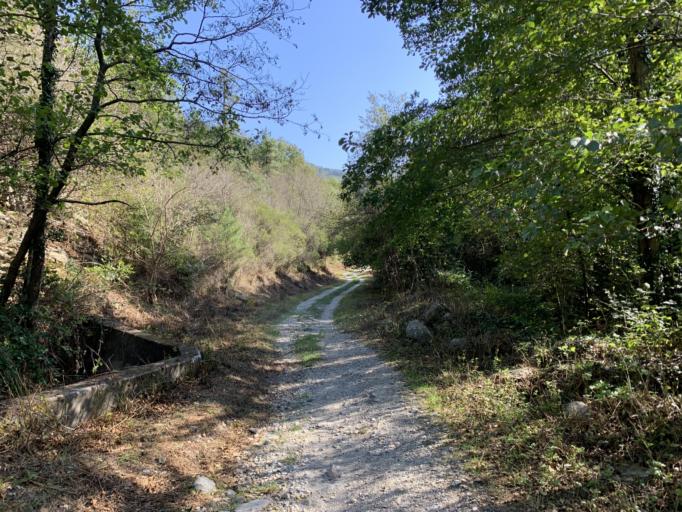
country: IT
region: Liguria
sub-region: Provincia di Savona
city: Magliolo
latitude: 44.2017
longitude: 8.2119
